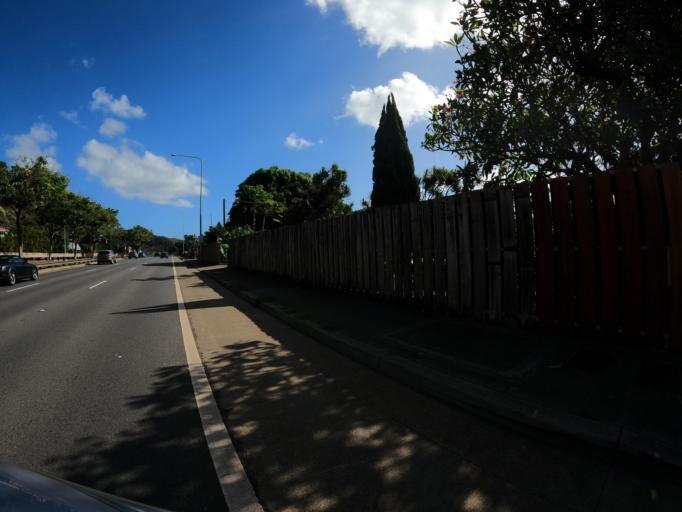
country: US
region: Hawaii
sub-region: Honolulu County
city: Waimanalo Beach
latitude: 21.2831
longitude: -157.7298
